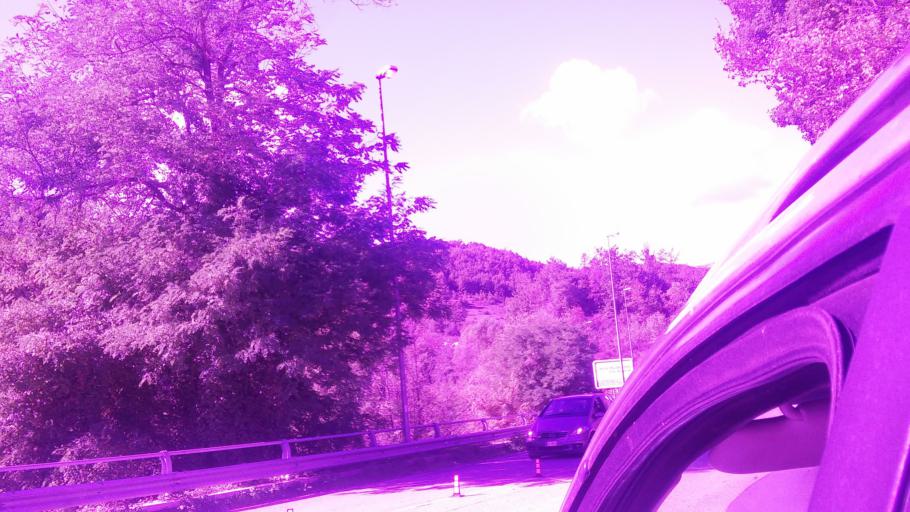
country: IT
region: Latium
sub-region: Provincia di Rieti
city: Amatrice
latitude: 42.6324
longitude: 13.2865
